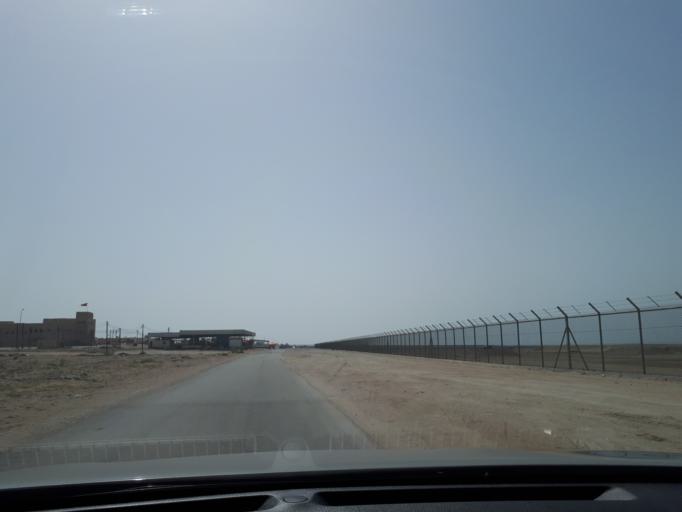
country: OM
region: Al Batinah
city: Barka'
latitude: 23.7094
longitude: 57.8980
